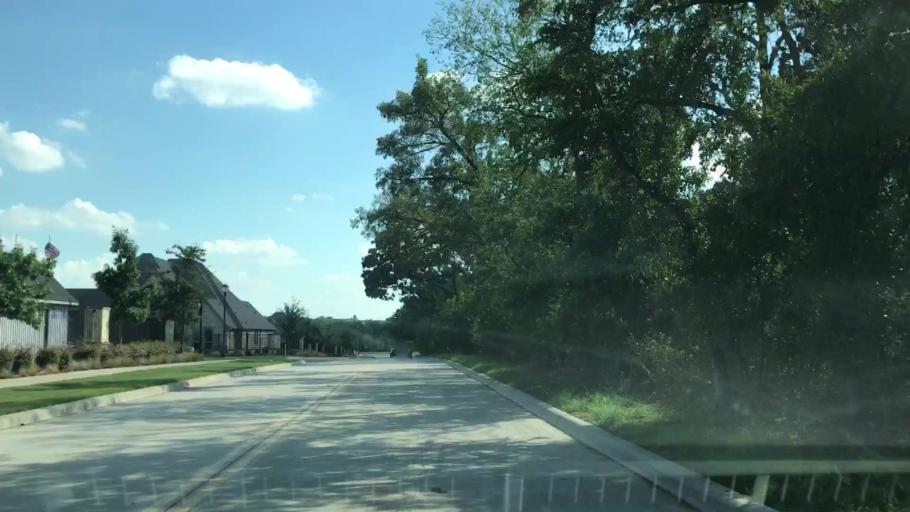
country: US
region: Texas
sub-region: Tarrant County
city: Keller
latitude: 32.9025
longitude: -97.2202
